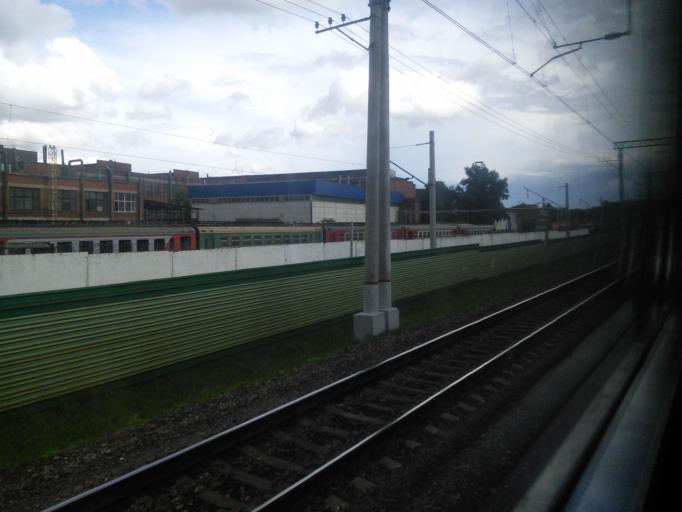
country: RU
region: Moscow
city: Ryazanskiy
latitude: 55.7421
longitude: 37.7446
